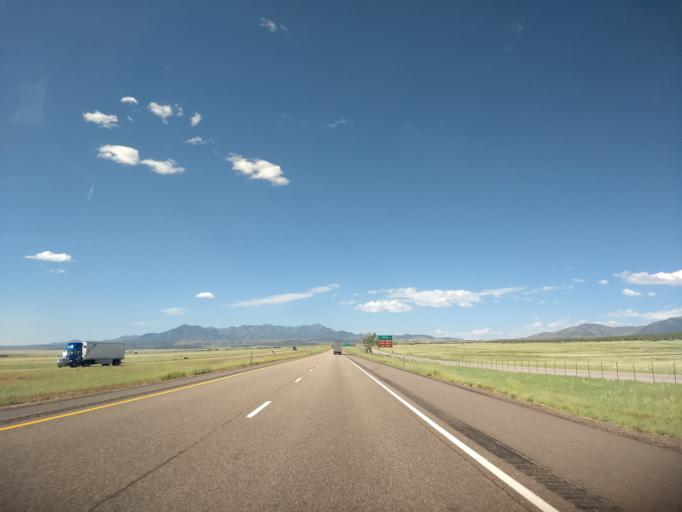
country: US
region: Utah
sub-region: Millard County
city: Fillmore
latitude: 39.0675
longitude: -112.2833
